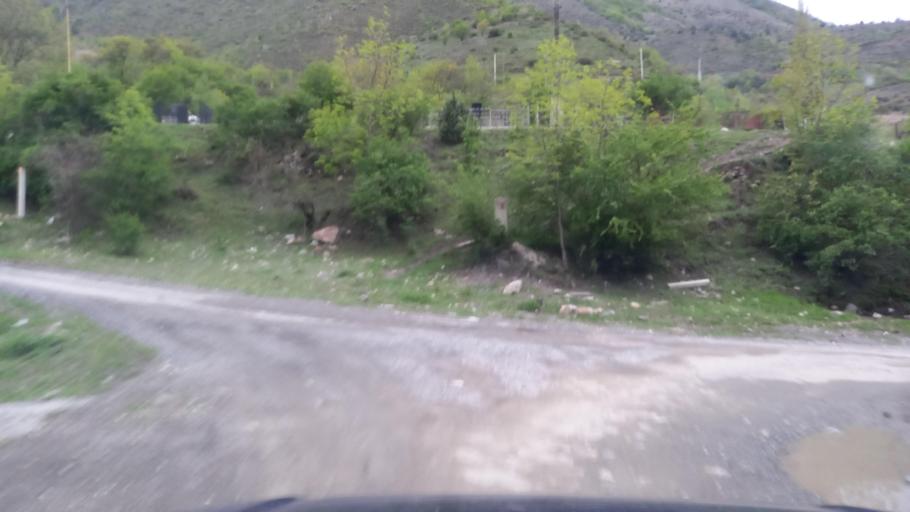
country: RU
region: North Ossetia
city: Mizur
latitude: 42.8488
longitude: 44.1569
